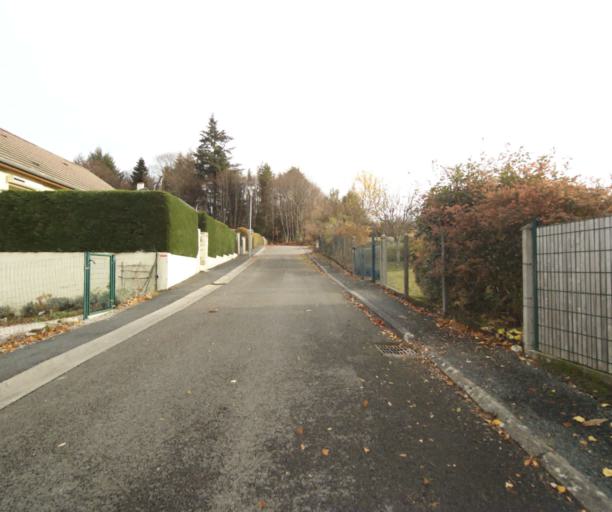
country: FR
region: Limousin
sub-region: Departement de la Correze
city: Sainte-Fortunade
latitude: 45.2016
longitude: 1.7728
